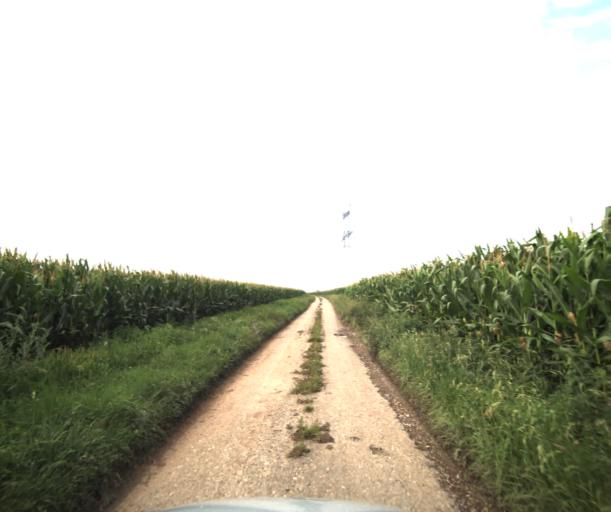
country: FR
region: Midi-Pyrenees
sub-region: Departement de la Haute-Garonne
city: Longages
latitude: 43.3862
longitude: 1.2351
